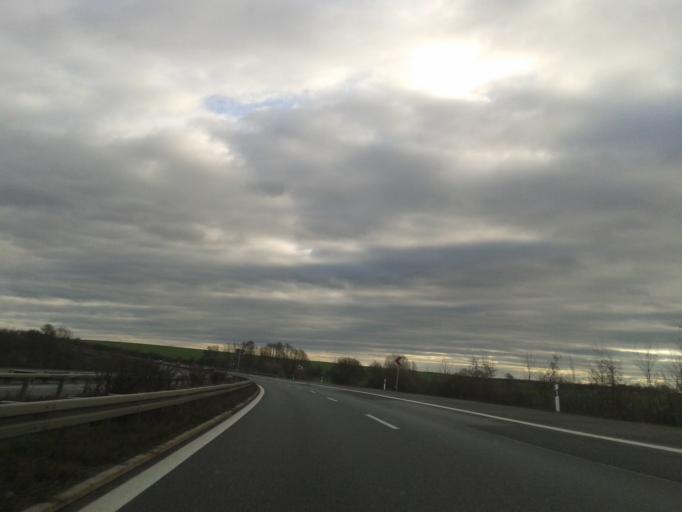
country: DE
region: Saxony
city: Wachau
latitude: 51.1608
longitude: 13.9290
